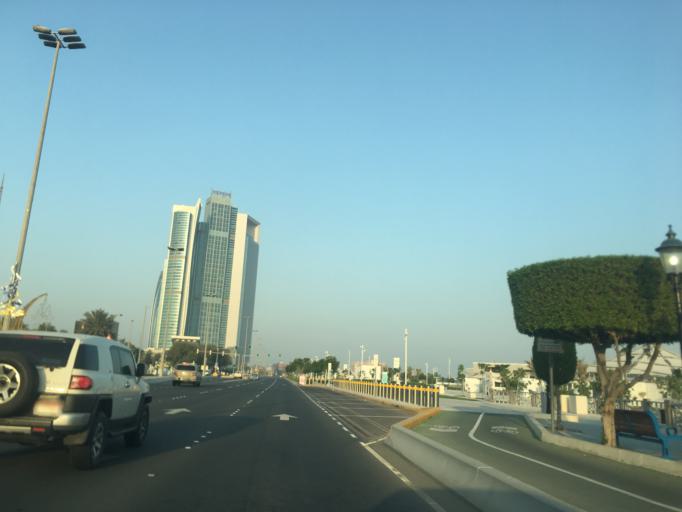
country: AE
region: Abu Dhabi
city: Abu Dhabi
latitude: 24.4690
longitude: 54.3340
